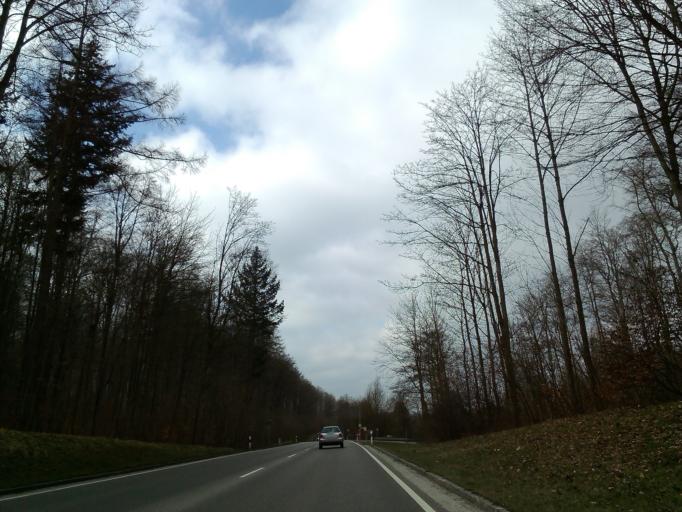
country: DE
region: Bavaria
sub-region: Swabia
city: Krumbach
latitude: 48.2451
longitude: 10.3954
